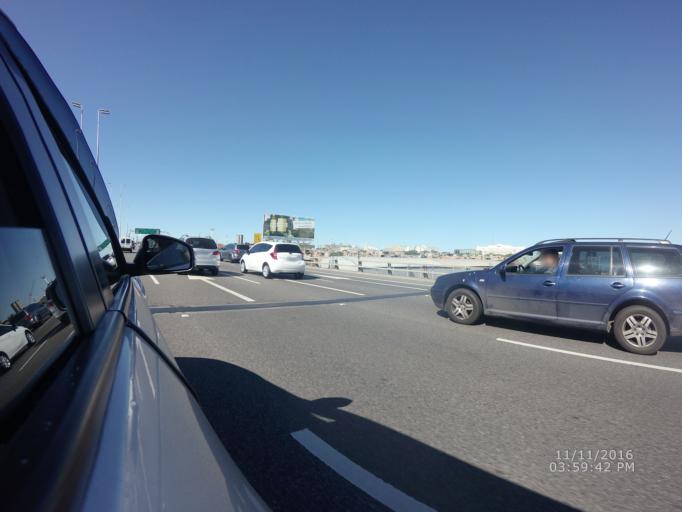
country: AR
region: Buenos Aires F.D.
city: Retiro
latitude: -34.5870
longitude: -58.3806
